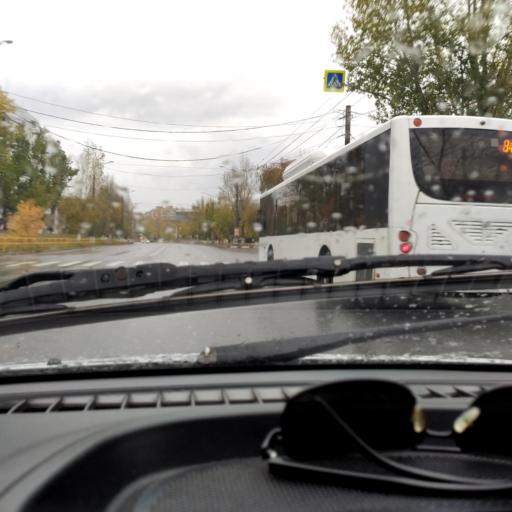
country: RU
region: Samara
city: Zhigulevsk
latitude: 53.4819
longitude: 49.4684
